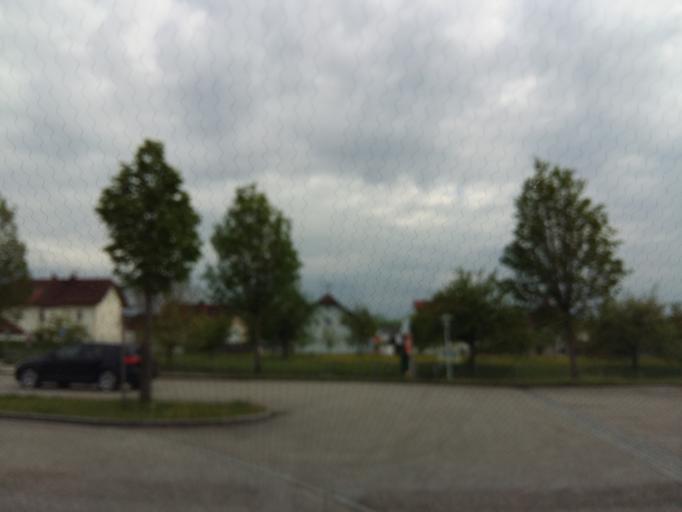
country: AT
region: Upper Austria
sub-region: Politischer Bezirk Scharding
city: Sankt Marienkirchen bei Schaerding
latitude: 48.3895
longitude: 13.4538
